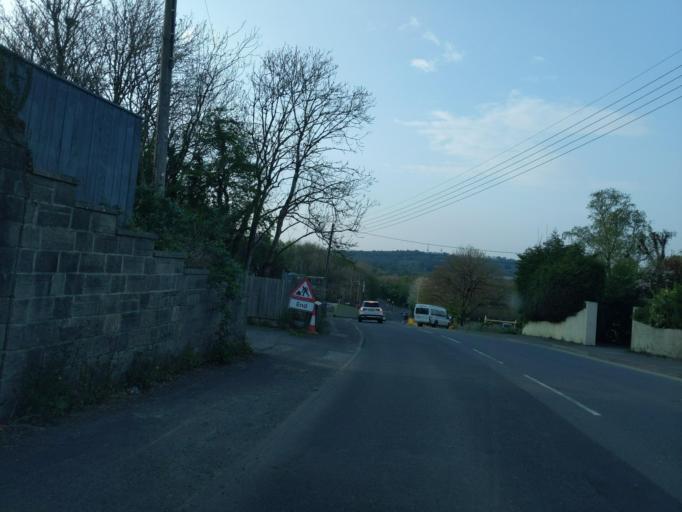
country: GB
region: England
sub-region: Plymouth
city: Plymstock
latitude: 50.3632
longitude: -4.0654
